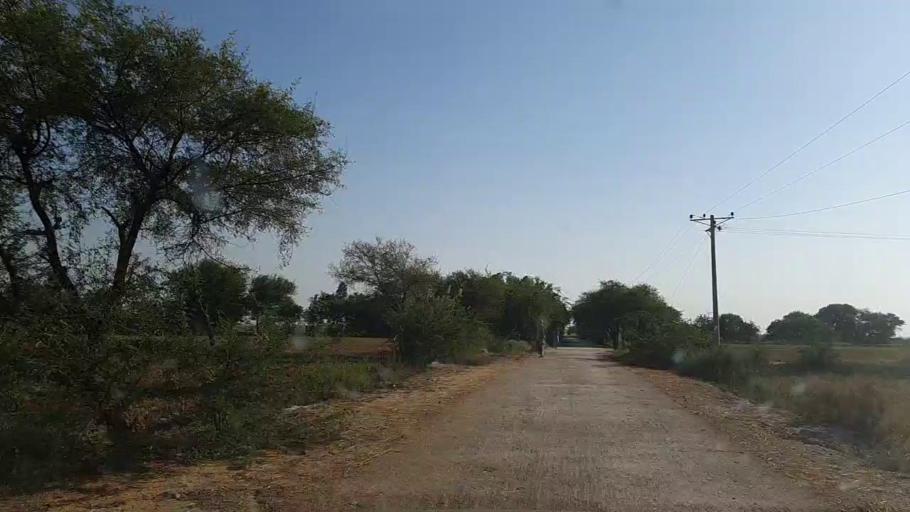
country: PK
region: Sindh
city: Daro Mehar
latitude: 24.6462
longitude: 68.0751
